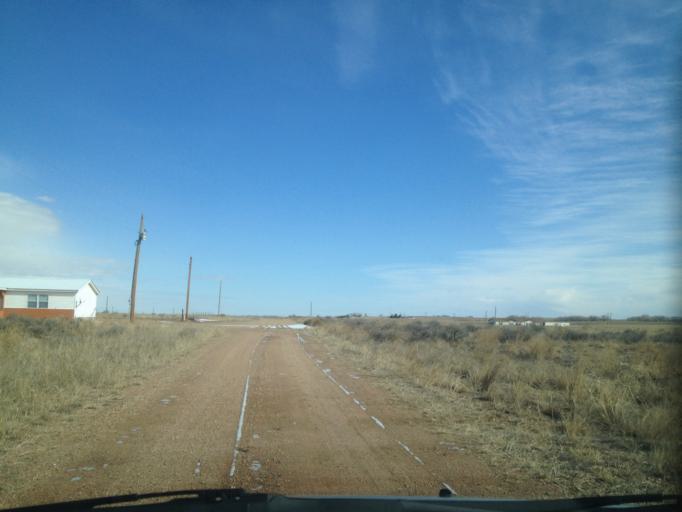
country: US
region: Colorado
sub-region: Weld County
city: Keenesburg
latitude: 40.2874
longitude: -104.2584
